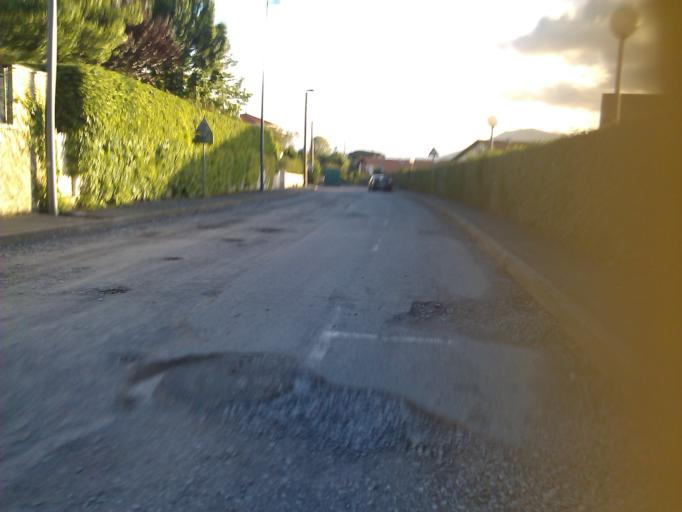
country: FR
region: Aquitaine
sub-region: Departement des Pyrenees-Atlantiques
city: Hendaye
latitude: 43.3698
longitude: -1.7618
